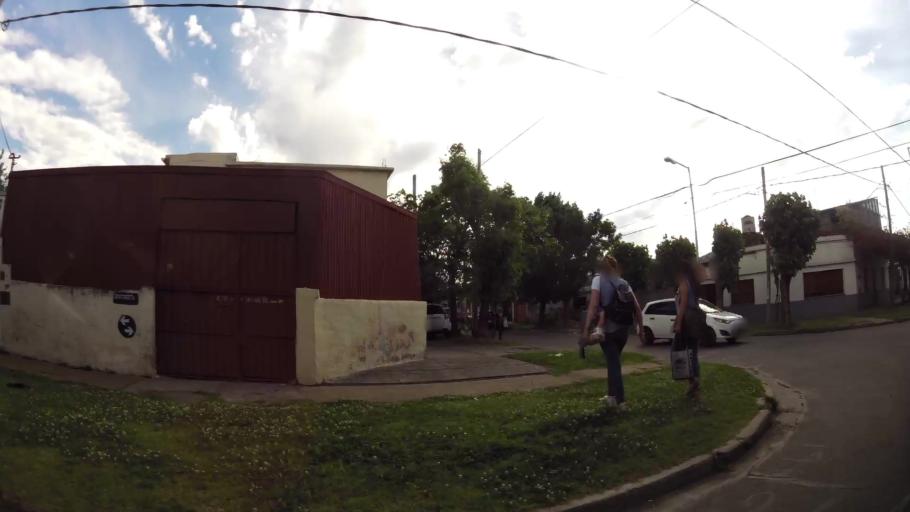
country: AR
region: Buenos Aires
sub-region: Partido de Avellaneda
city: Avellaneda
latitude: -34.6894
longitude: -58.3659
